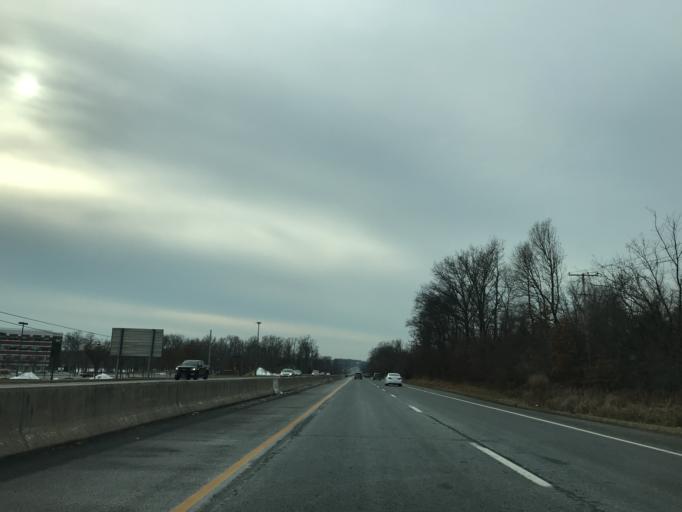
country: US
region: Maryland
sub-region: Harford County
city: Riverside
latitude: 39.4697
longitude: -76.2372
